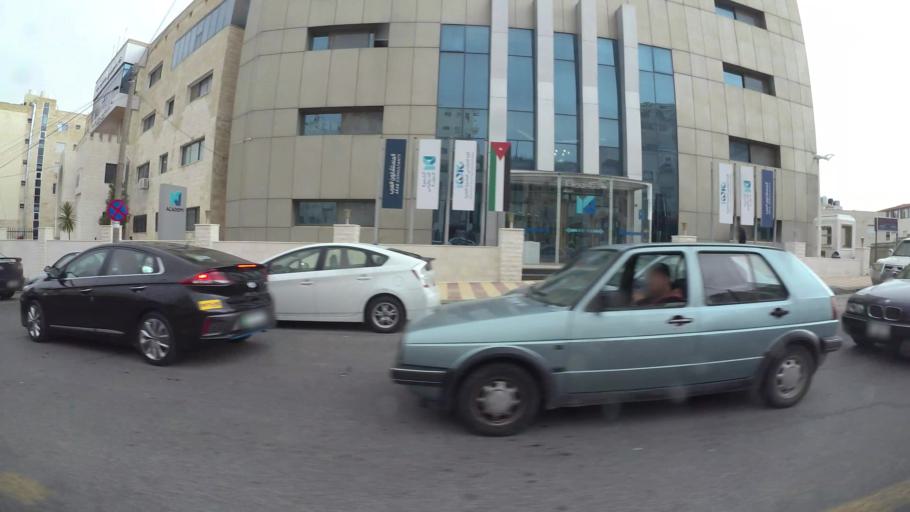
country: JO
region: Amman
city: Al Jubayhah
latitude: 31.9926
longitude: 35.8594
